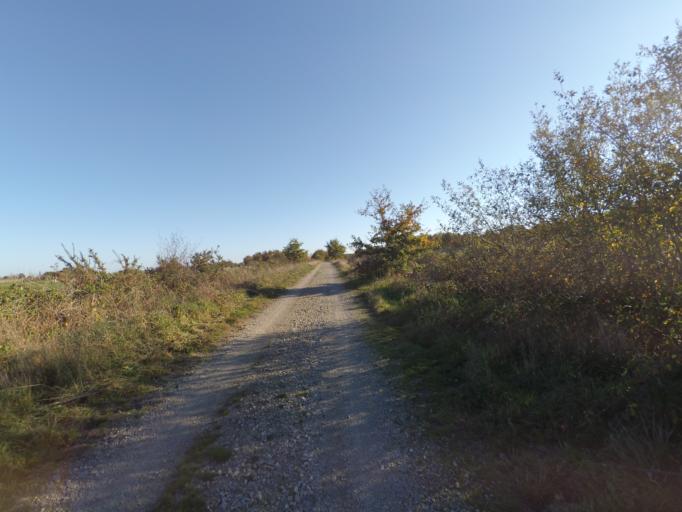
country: FR
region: Pays de la Loire
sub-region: Departement de la Loire-Atlantique
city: La Planche
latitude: 47.0236
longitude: -1.3995
